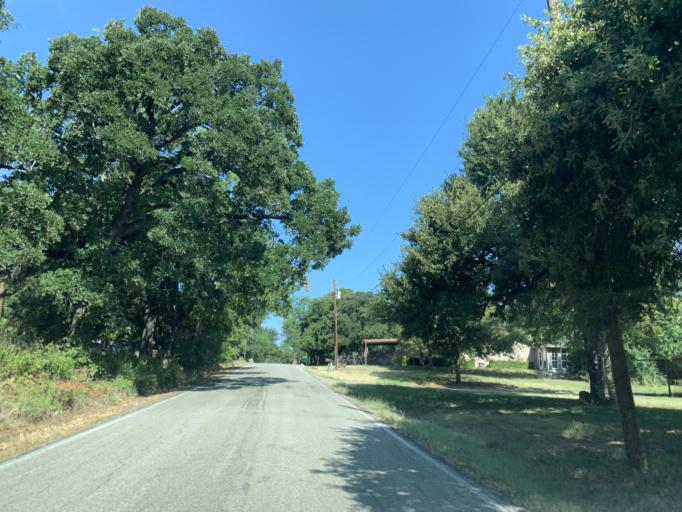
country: US
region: Texas
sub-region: Tarrant County
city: Azle
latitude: 32.8621
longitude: -97.5239
